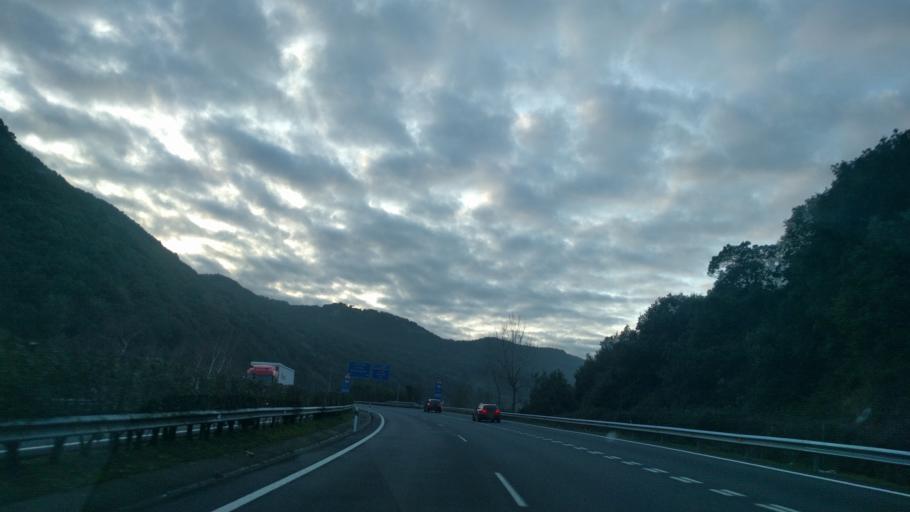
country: ES
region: Cantabria
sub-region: Provincia de Cantabria
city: Liendo
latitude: 43.3908
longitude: -3.3390
